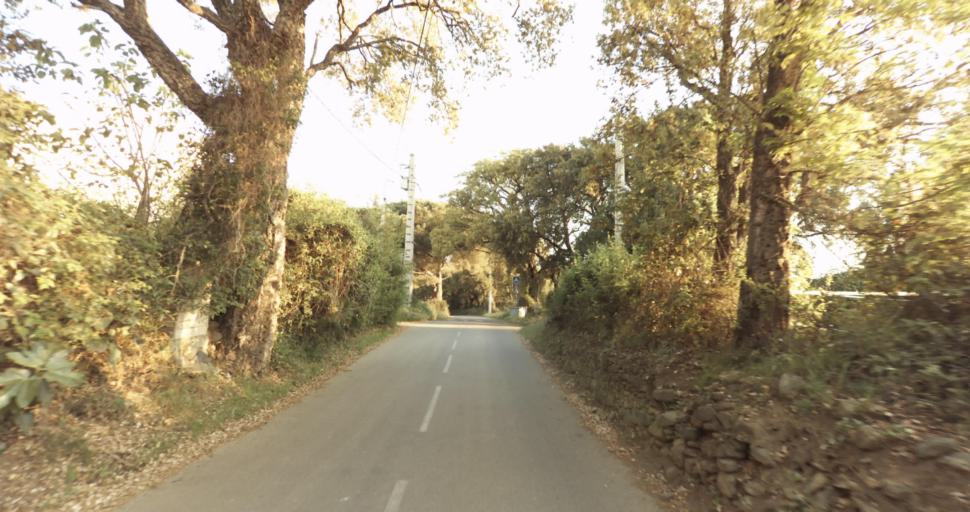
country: FR
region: Corsica
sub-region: Departement de la Haute-Corse
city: Biguglia
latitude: 42.6231
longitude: 9.4439
